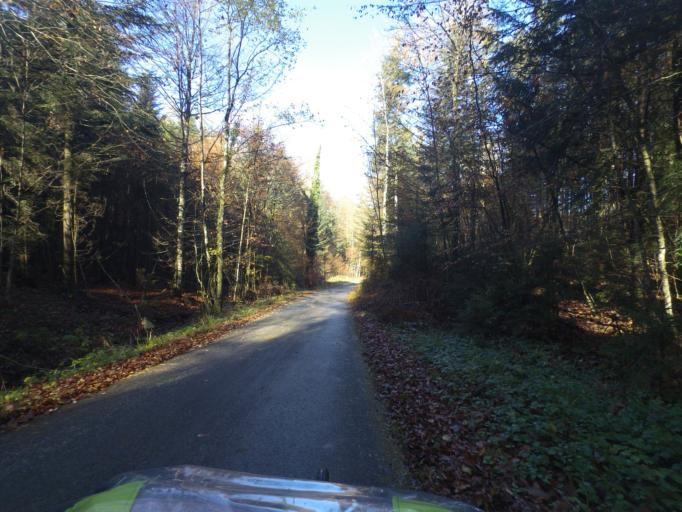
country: AT
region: Salzburg
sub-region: Politischer Bezirk Hallein
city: Adnet
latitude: 47.6744
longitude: 13.1577
